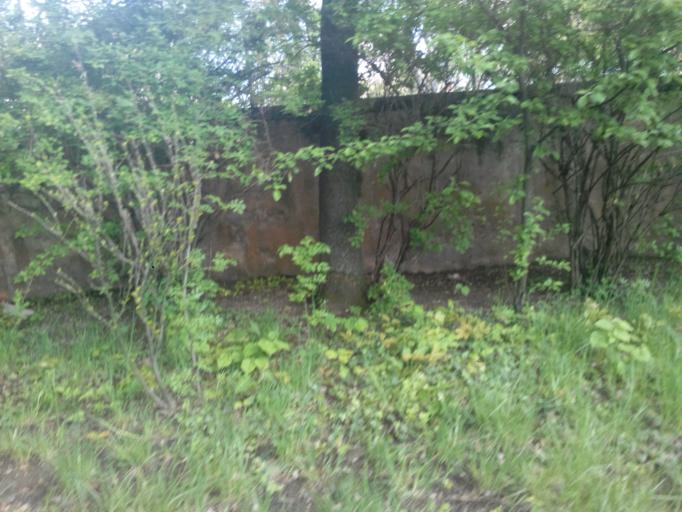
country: RO
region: Bucuresti
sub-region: Municipiul Bucuresti
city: Bucuresti
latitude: 44.4360
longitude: 26.0641
